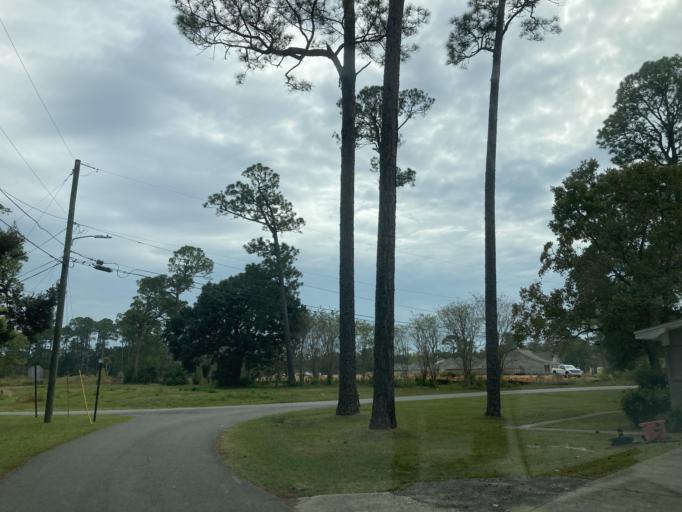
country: US
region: Mississippi
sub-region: Jackson County
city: Gulf Hills
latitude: 30.4369
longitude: -88.8391
